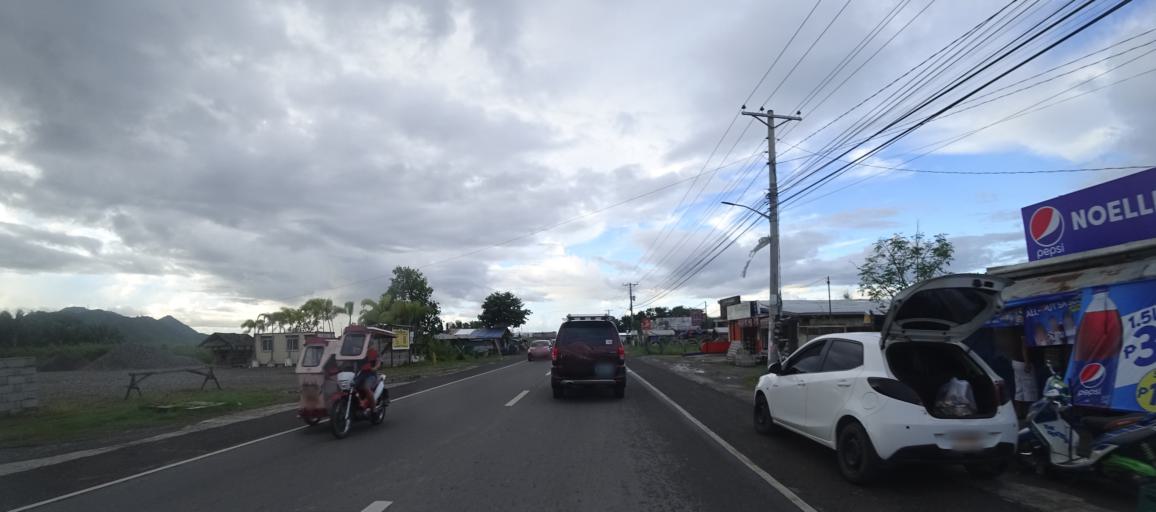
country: PH
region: Eastern Visayas
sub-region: Province of Leyte
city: Pawing
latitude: 11.1734
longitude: 124.9996
